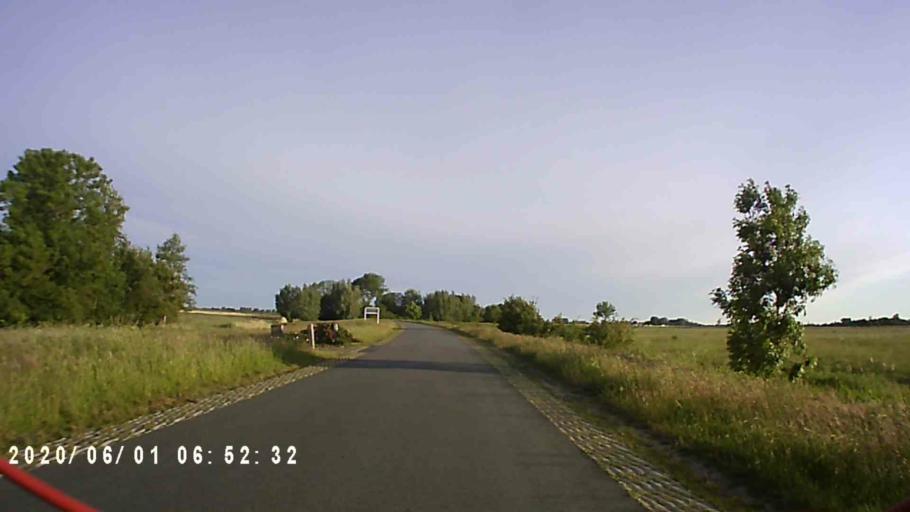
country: NL
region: Friesland
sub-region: Gemeente Kollumerland en Nieuwkruisland
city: Kollum
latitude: 53.3090
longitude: 6.1308
